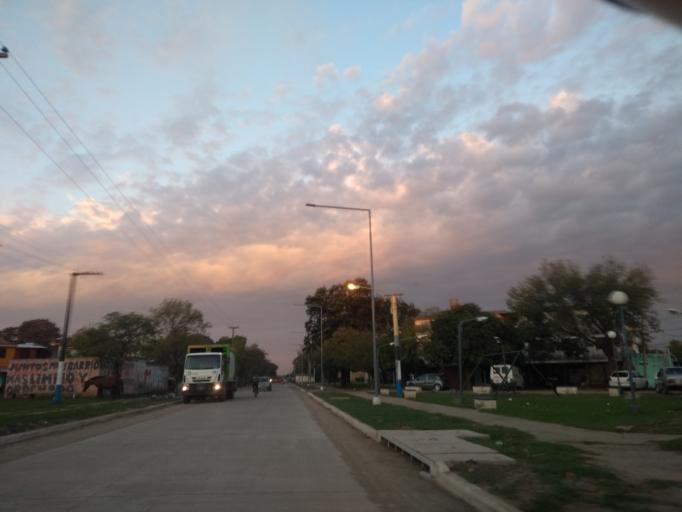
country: AR
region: Chaco
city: Resistencia
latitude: -27.4840
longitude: -58.9872
